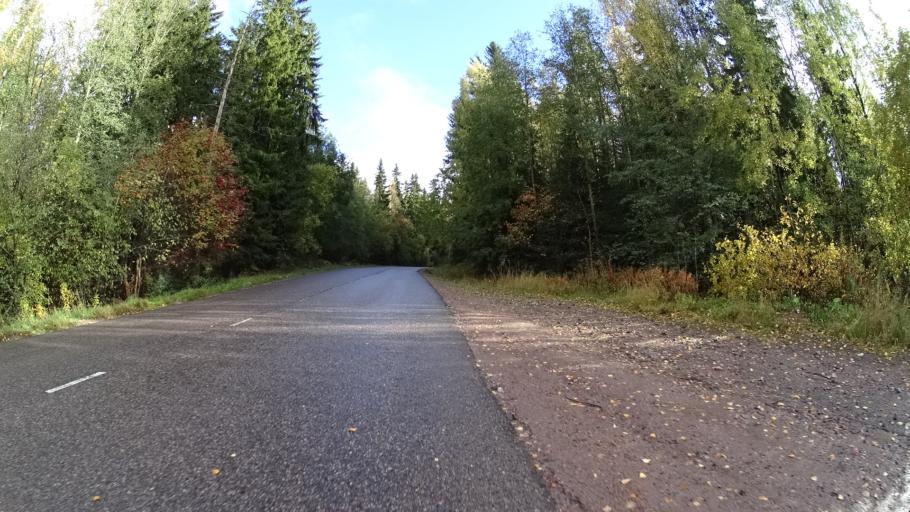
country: FI
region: Uusimaa
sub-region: Helsinki
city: Kilo
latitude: 60.2889
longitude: 24.8063
